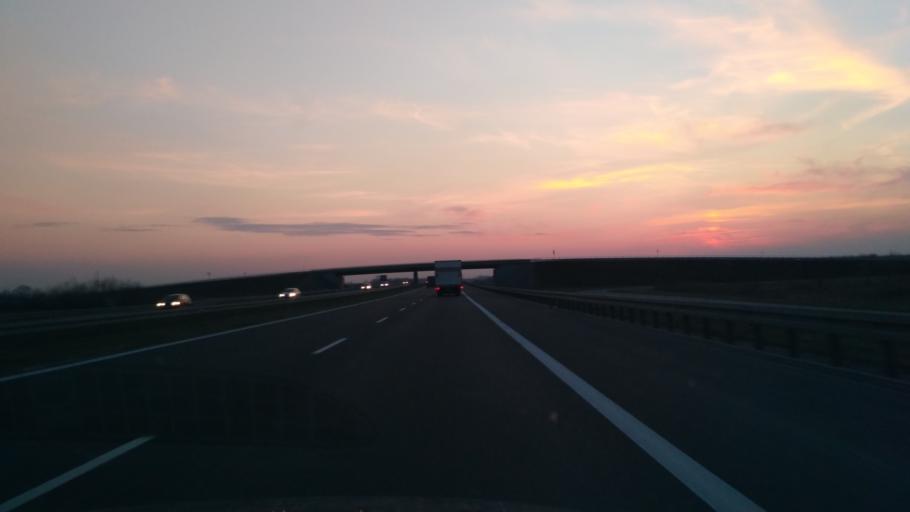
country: PL
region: Subcarpathian Voivodeship
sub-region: Powiat rzeszowski
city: Wolka Podlesna
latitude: 50.0950
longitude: 22.1031
